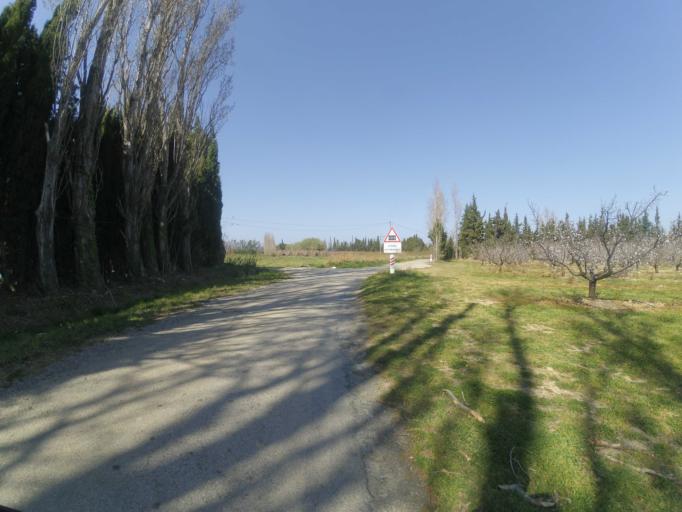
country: FR
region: Languedoc-Roussillon
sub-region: Departement des Pyrenees-Orientales
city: Pezilla-la-Riviere
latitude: 42.6739
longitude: 2.7548
